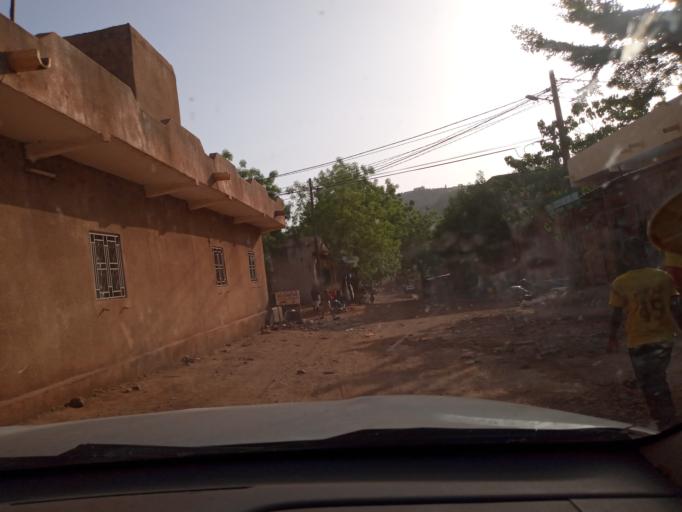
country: ML
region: Bamako
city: Bamako
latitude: 12.6704
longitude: -7.9758
